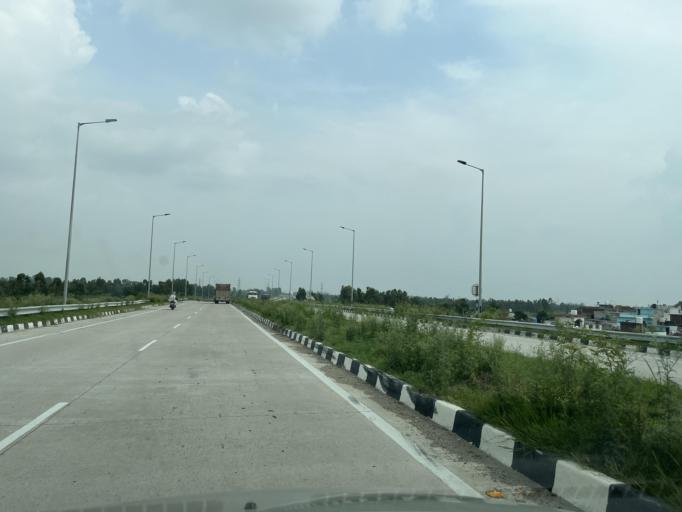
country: IN
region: Uttarakhand
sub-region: Udham Singh Nagar
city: Kashipur
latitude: 29.1727
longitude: 78.9484
